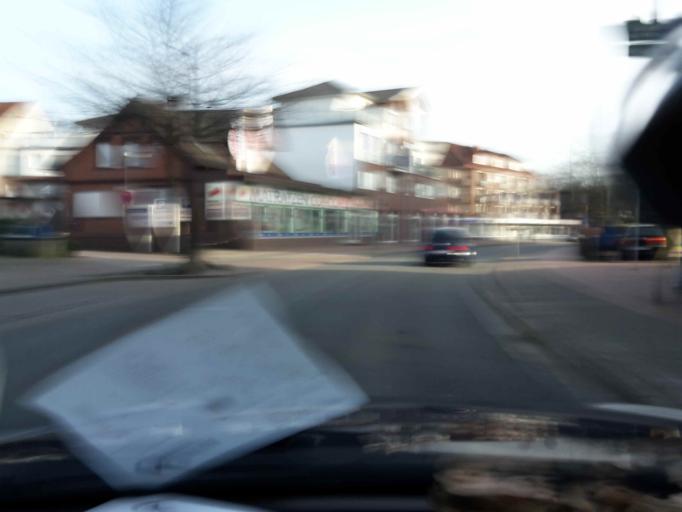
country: DE
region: Lower Saxony
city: Buchholz in der Nordheide
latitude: 53.3286
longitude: 9.8823
